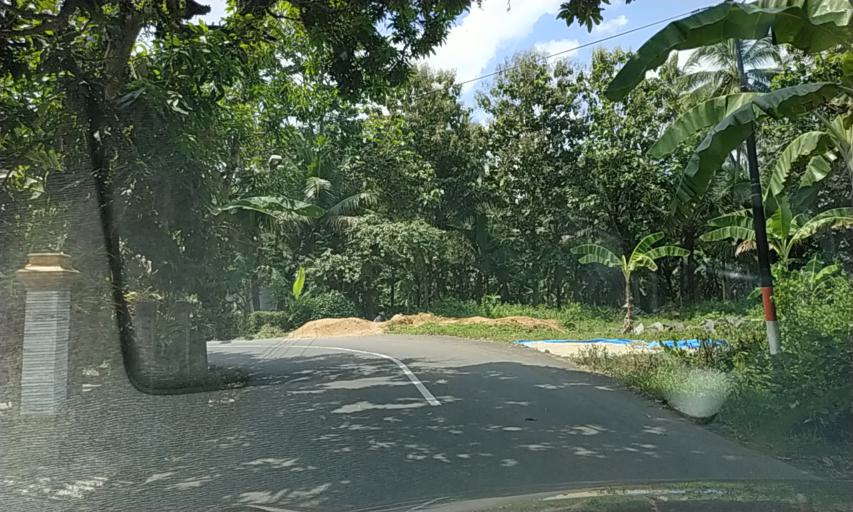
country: ID
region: Central Java
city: Gombong
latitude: -7.6280
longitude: 109.7215
